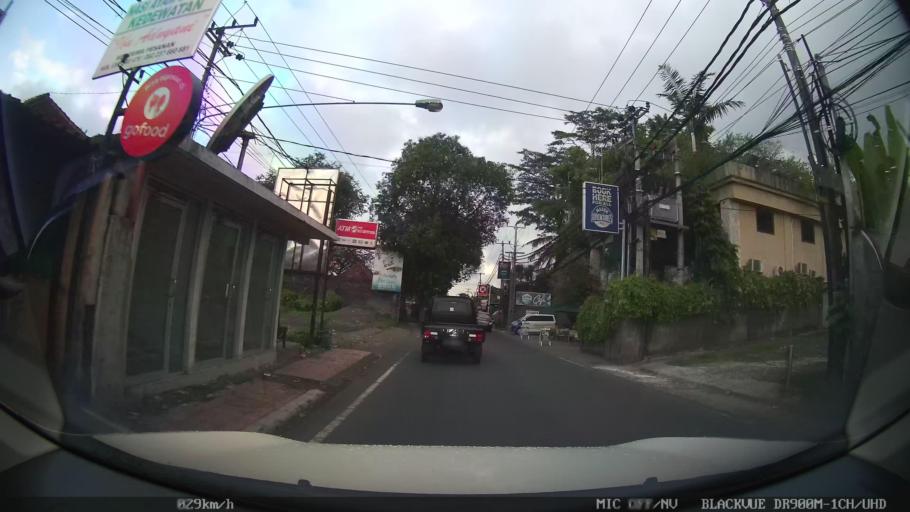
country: ID
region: Bali
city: Bunutan
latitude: -8.4797
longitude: 115.2476
